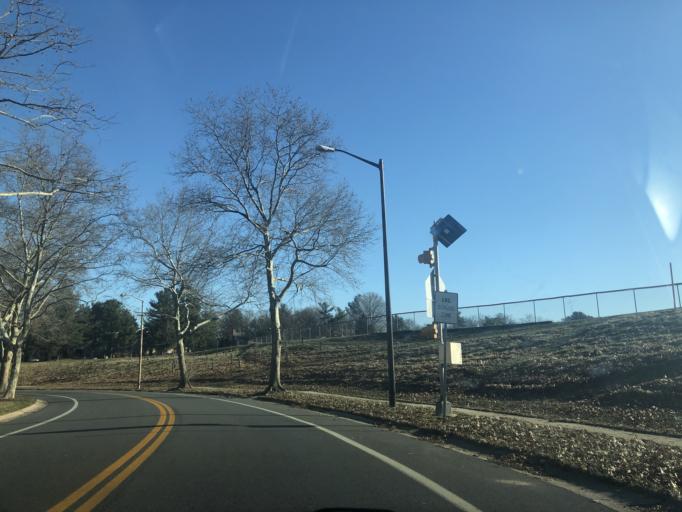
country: US
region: Maryland
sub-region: Howard County
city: Columbia
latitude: 39.2098
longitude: -76.8430
